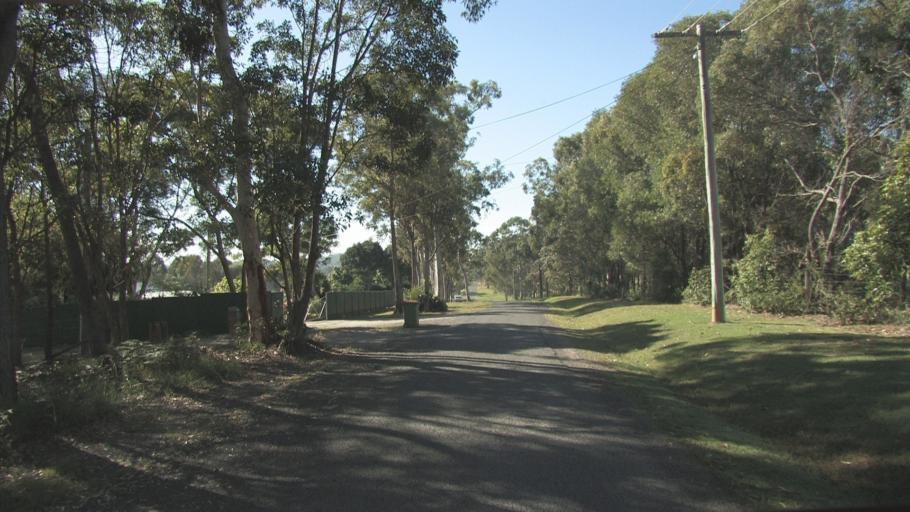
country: AU
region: Queensland
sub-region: Gold Coast
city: Yatala
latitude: -27.6899
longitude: 153.2830
